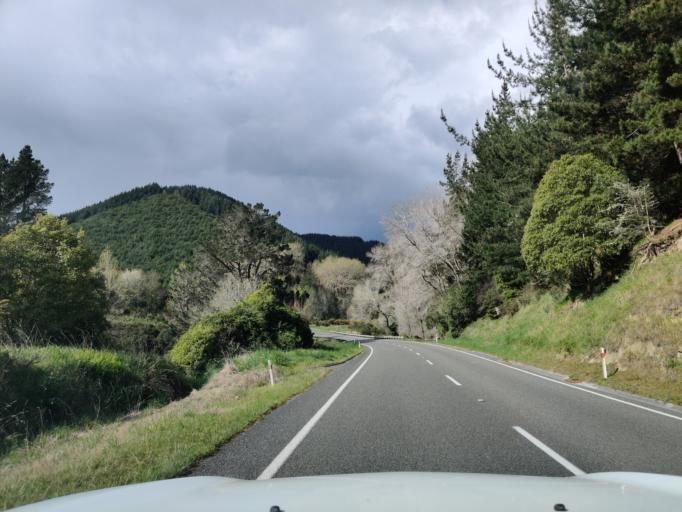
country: NZ
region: Manawatu-Wanganui
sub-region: Wanganui District
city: Wanganui
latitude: -39.8140
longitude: 175.1856
